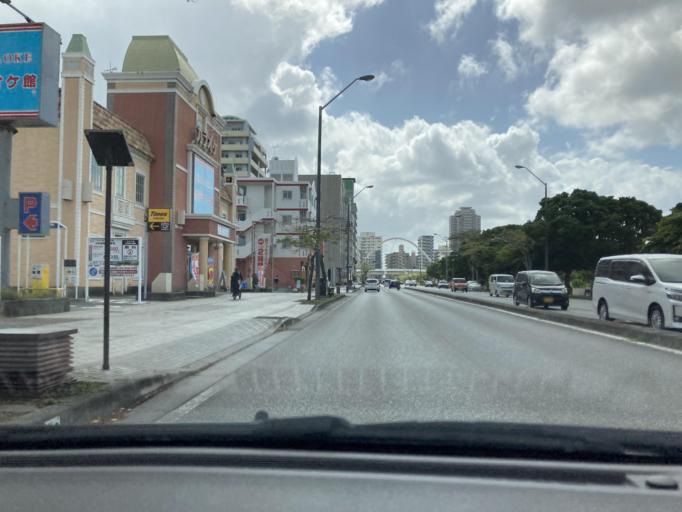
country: JP
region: Okinawa
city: Naha-shi
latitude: 26.2288
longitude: 127.6975
